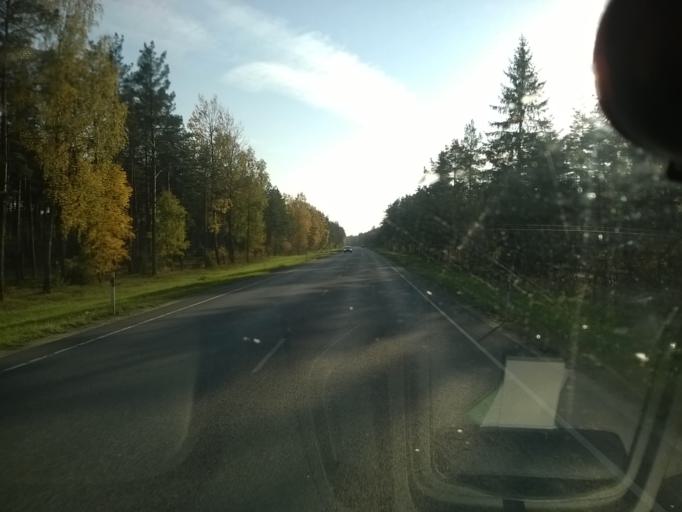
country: EE
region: Harju
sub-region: Saku vald
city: Saku
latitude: 59.3271
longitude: 24.6921
